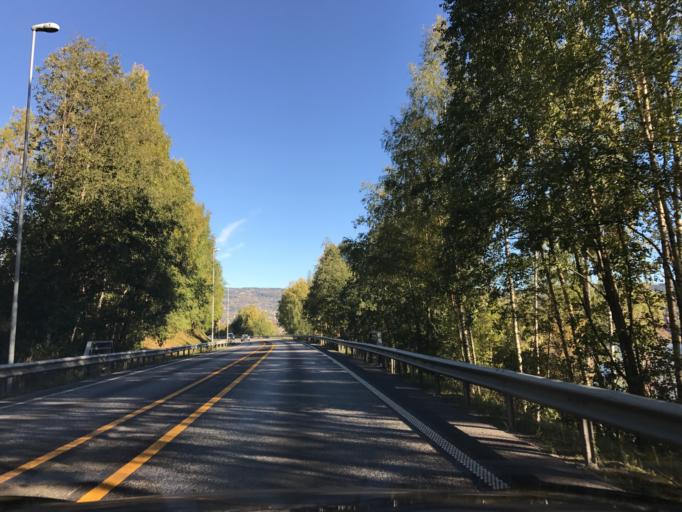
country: NO
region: Oppland
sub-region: Lillehammer
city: Lillehammer
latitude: 61.0975
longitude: 10.4375
